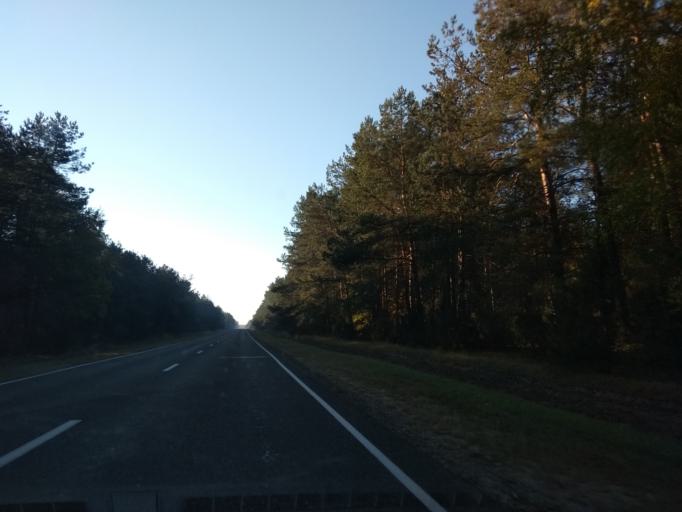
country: BY
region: Brest
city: Kobryn
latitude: 52.0896
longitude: 24.2794
